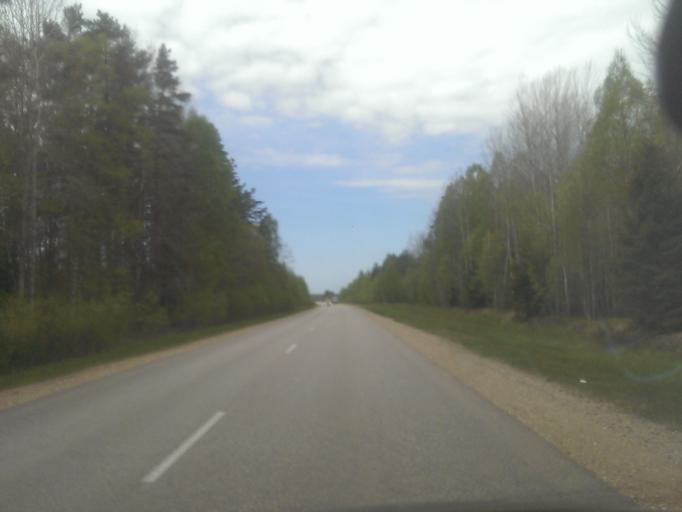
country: LV
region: Ventspils Rajons
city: Piltene
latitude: 57.1650
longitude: 21.6837
